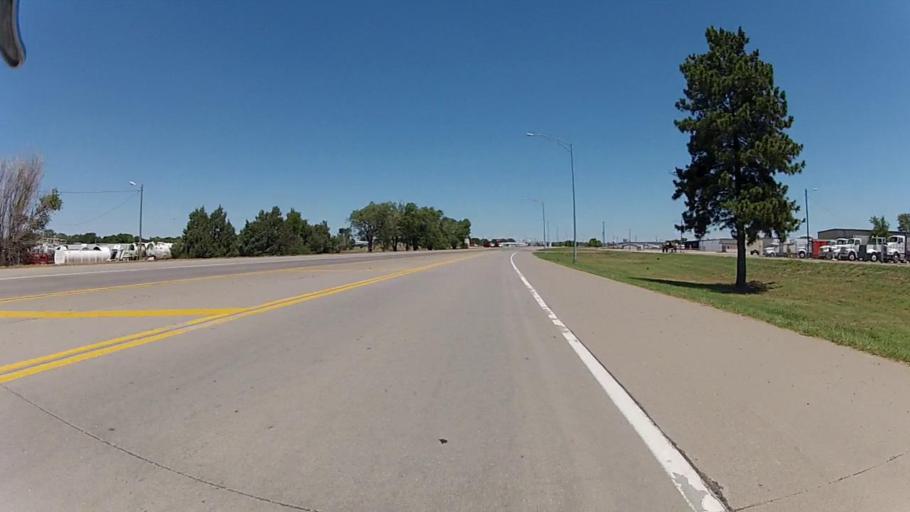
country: US
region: Kansas
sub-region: Ford County
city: Dodge City
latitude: 37.7303
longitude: -100.0188
